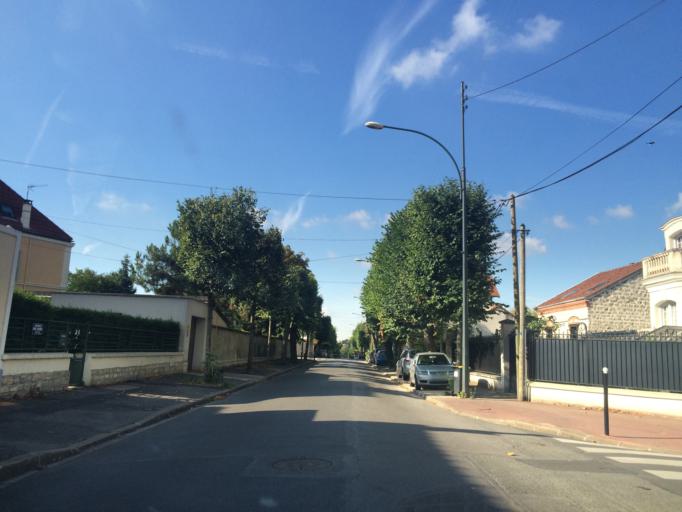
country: FR
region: Ile-de-France
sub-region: Departement du Val-de-Marne
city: Champigny-sur-Marne
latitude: 48.8053
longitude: 2.4950
